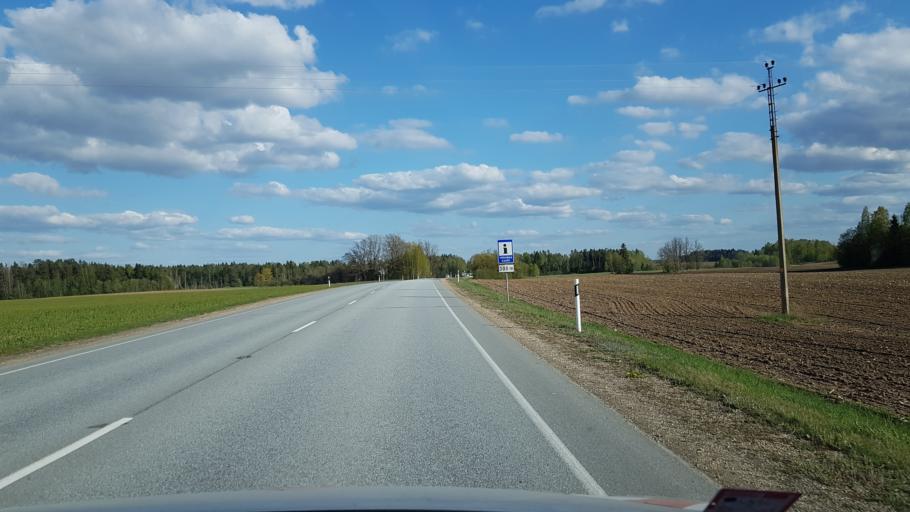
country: EE
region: Vorumaa
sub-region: Voru linn
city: Voru
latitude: 57.9069
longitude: 26.8301
